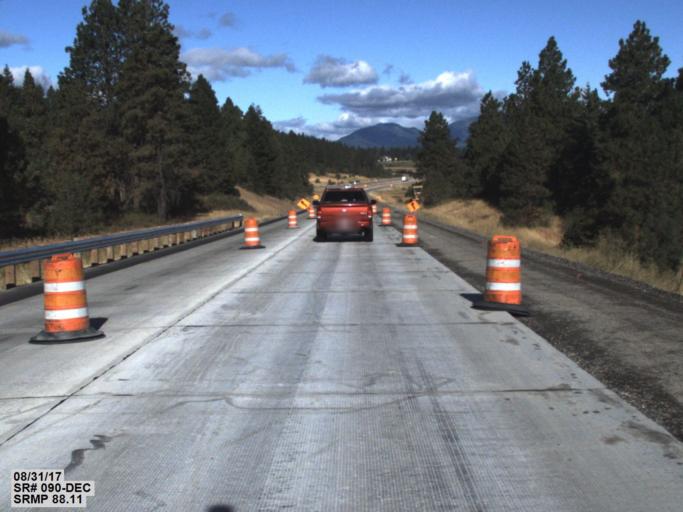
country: US
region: Washington
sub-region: Kittitas County
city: Cle Elum
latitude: 47.1627
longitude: -120.8669
